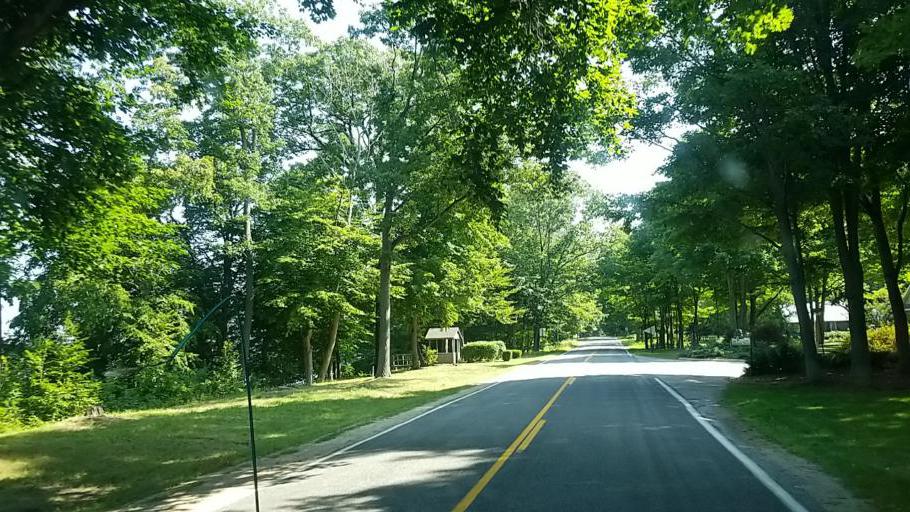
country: US
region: Michigan
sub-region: Muskegon County
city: Montague
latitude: 43.3636
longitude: -86.4062
